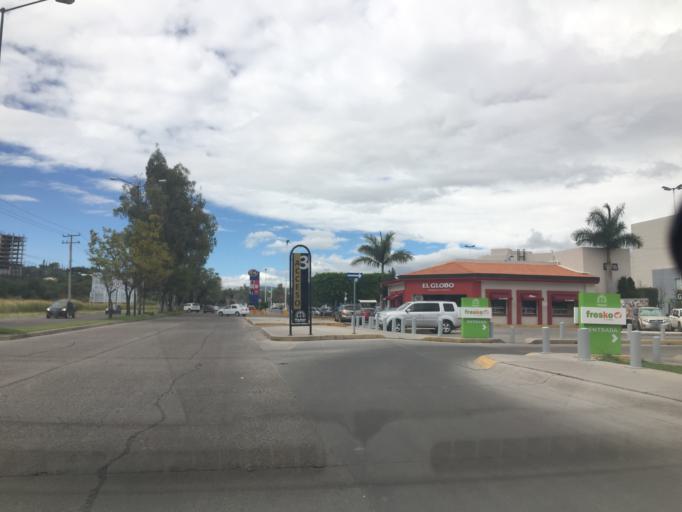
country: MX
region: Guanajuato
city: Leon
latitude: 21.1550
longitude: -101.6970
